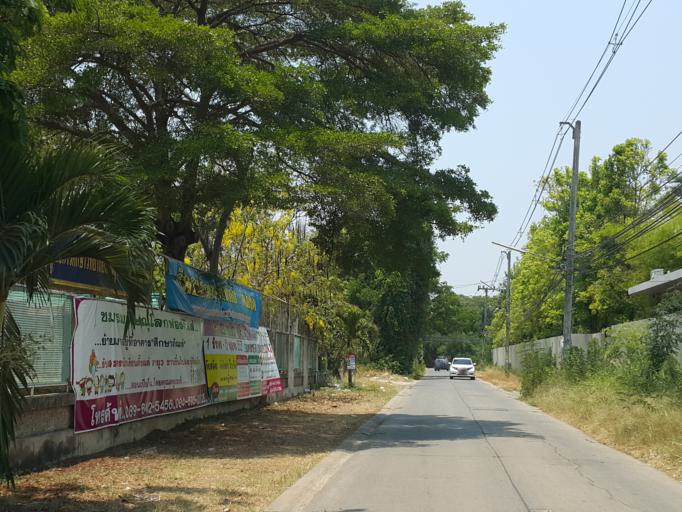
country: TH
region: Phitsanulok
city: Phitsanulok
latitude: 16.8158
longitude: 100.2463
